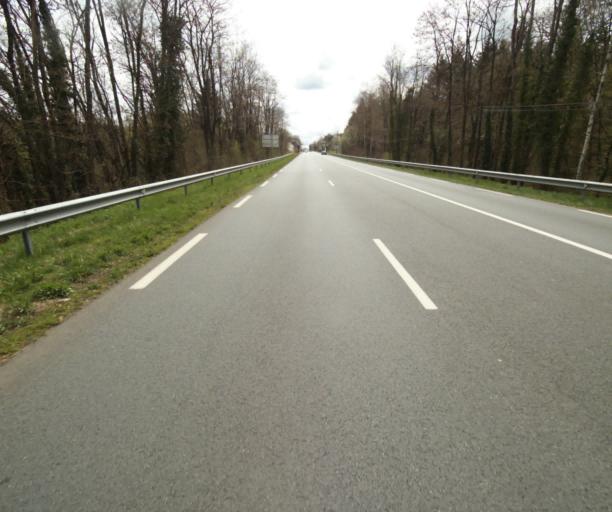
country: FR
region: Limousin
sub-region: Departement de la Correze
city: Sainte-Fortunade
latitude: 45.2043
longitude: 1.8285
